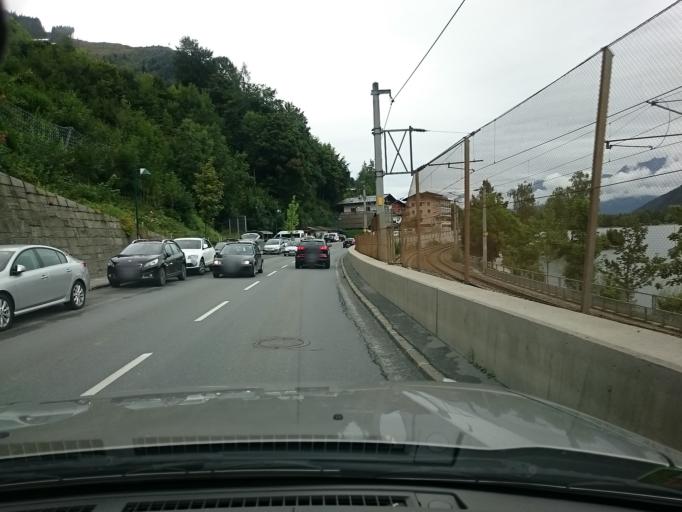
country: AT
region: Salzburg
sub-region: Politischer Bezirk Zell am See
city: Zell am See
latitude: 47.3321
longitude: 12.7969
